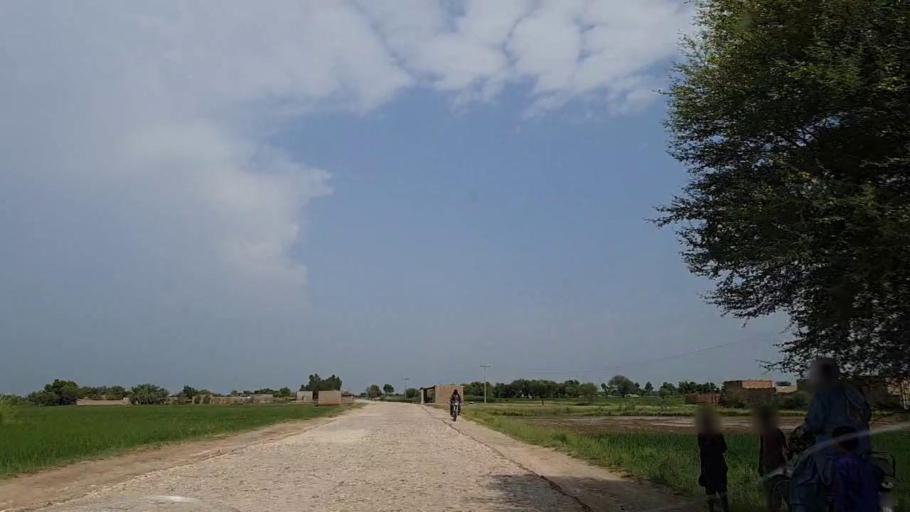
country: PK
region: Sindh
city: Khanpur
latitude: 27.8486
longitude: 69.4439
